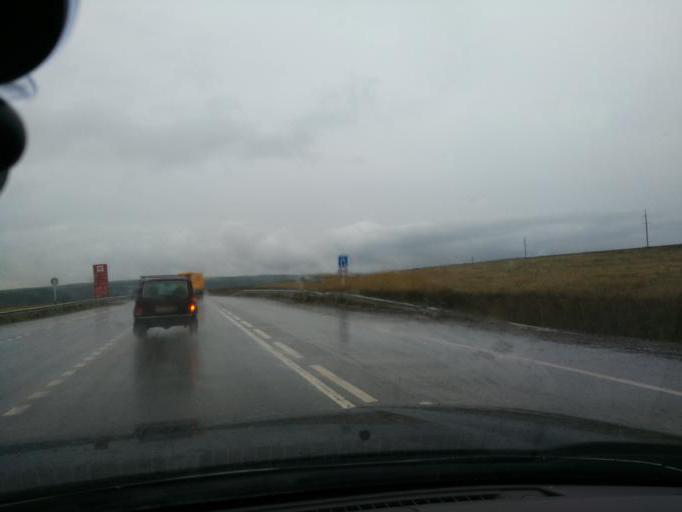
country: RU
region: Perm
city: Yugo-Kamskiy
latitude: 57.7022
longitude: 55.6250
